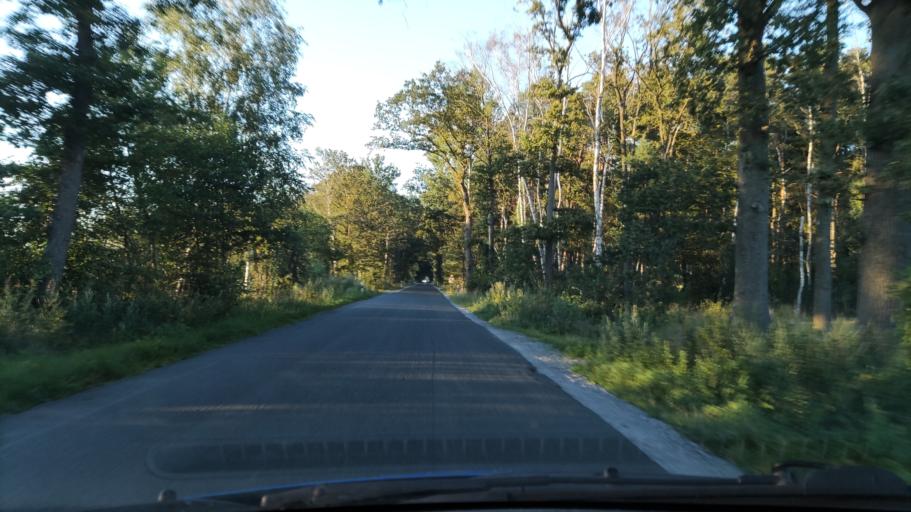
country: DE
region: Lower Saxony
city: Klein Gusborn
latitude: 53.0547
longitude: 11.1805
